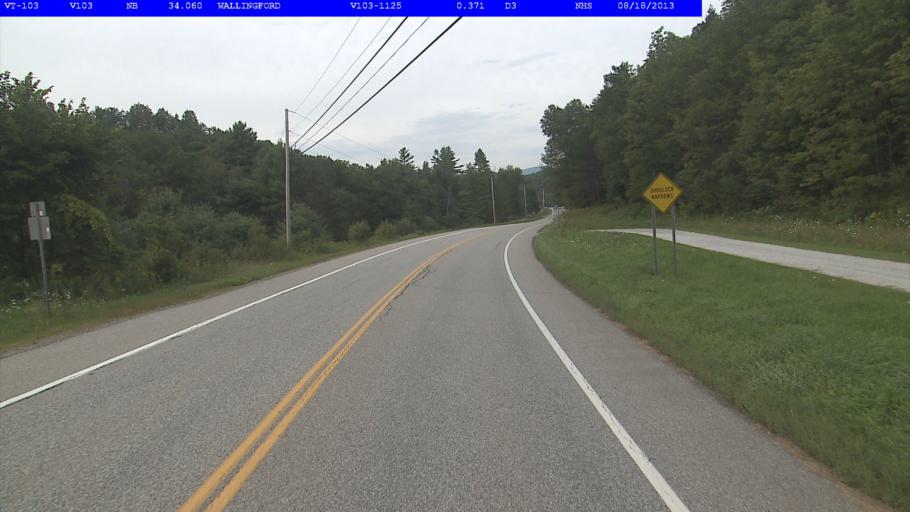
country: US
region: Vermont
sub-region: Rutland County
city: Rutland
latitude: 43.4520
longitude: -72.8782
